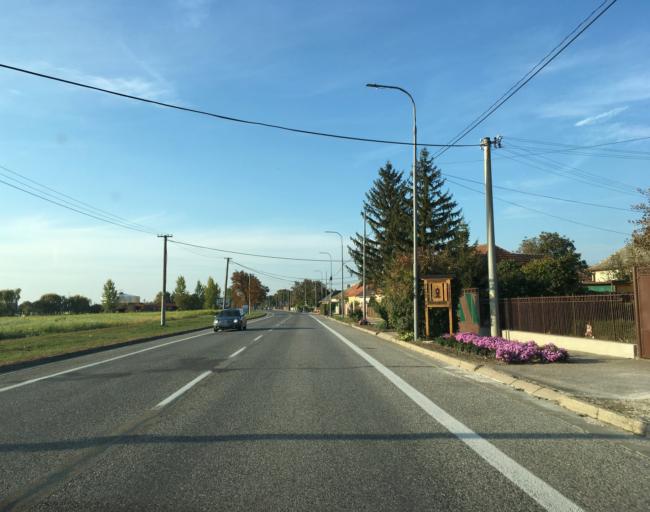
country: SK
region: Nitriansky
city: Surany
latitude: 48.0854
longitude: 18.0721
